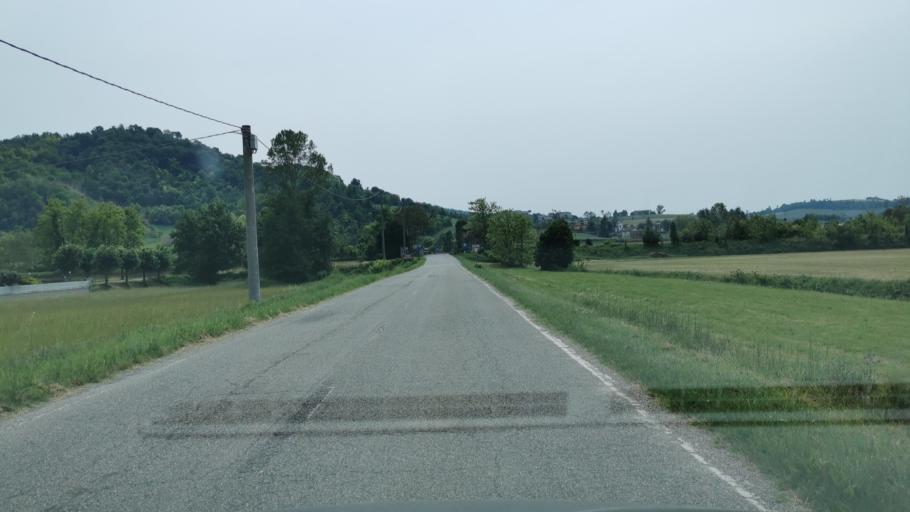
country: IT
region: Piedmont
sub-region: Provincia di Asti
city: Moncalvo
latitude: 45.0651
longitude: 8.2785
